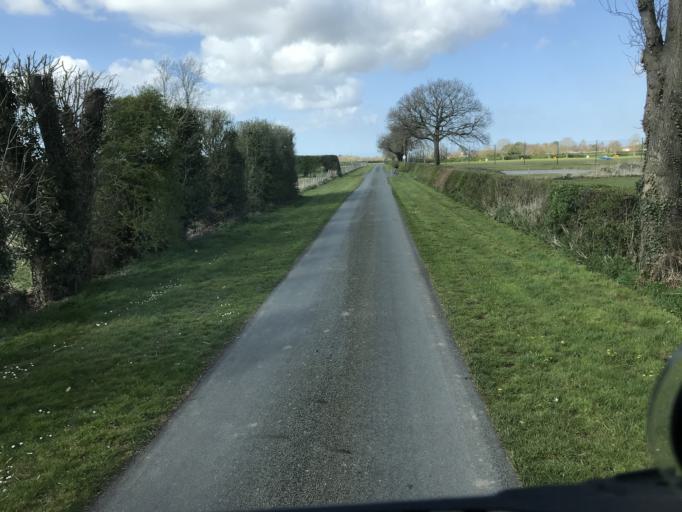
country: GB
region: England
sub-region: Cheshire West and Chester
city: Blacon
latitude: 53.1721
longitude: -2.9476
